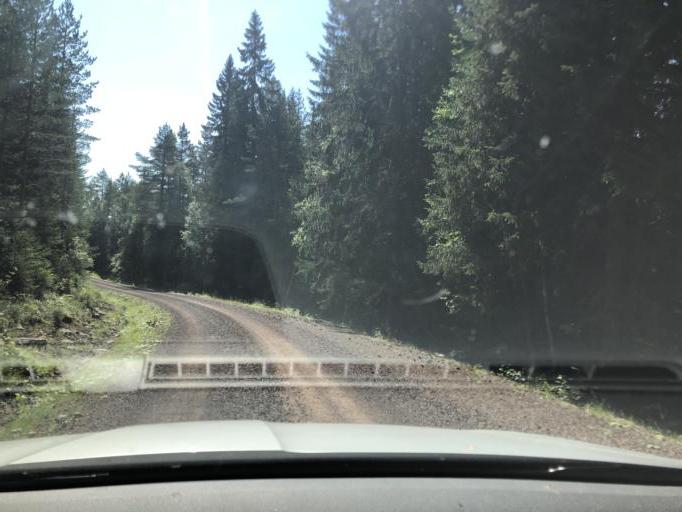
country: SE
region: Dalarna
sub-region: Orsa Kommun
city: Orsa
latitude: 61.2600
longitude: 14.7319
